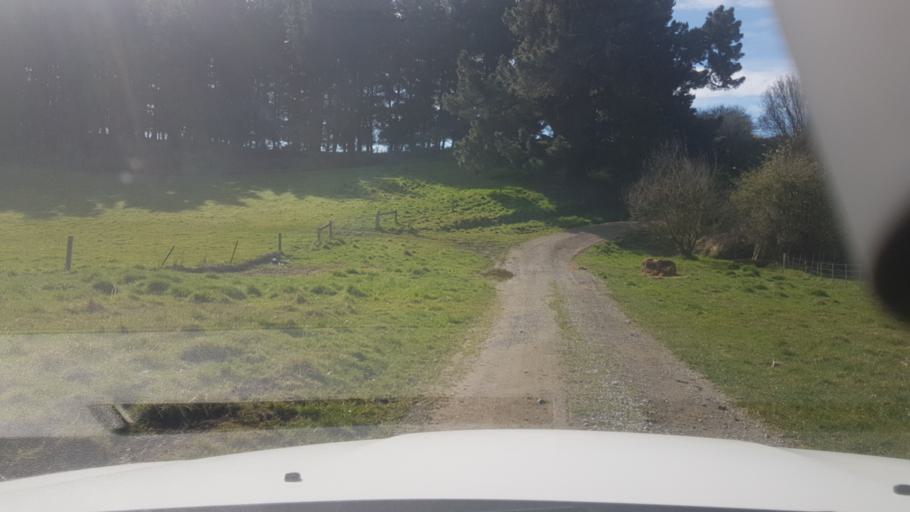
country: NZ
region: Canterbury
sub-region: Timaru District
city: Pleasant Point
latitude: -44.1963
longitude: 171.1876
